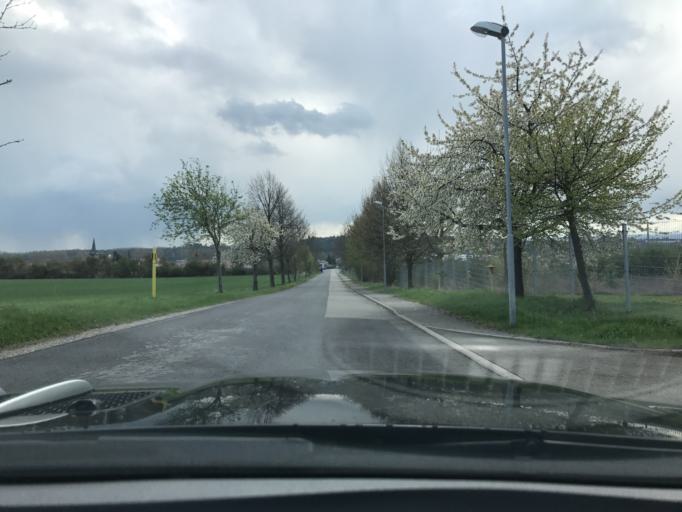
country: DE
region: Thuringia
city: Muehlhausen
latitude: 51.2175
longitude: 10.4919
